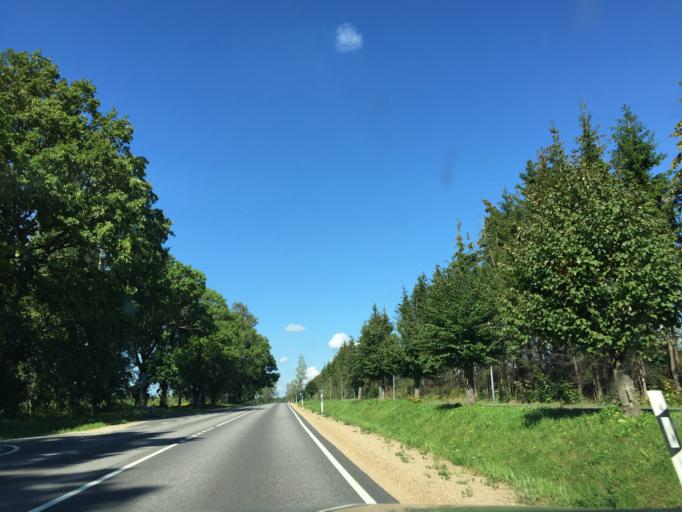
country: LV
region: Limbazu Rajons
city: Limbazi
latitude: 57.4915
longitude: 24.7088
